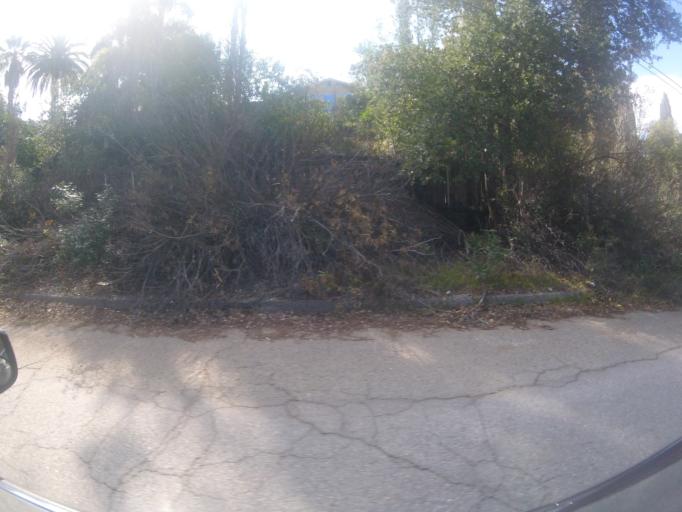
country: US
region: California
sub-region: San Bernardino County
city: Redlands
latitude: 34.0331
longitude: -117.1790
